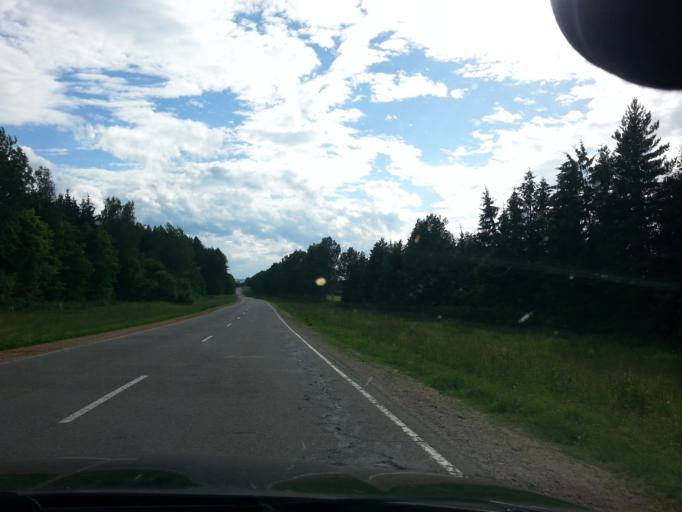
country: BY
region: Grodnenskaya
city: Astravyets
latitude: 54.7855
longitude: 26.0668
